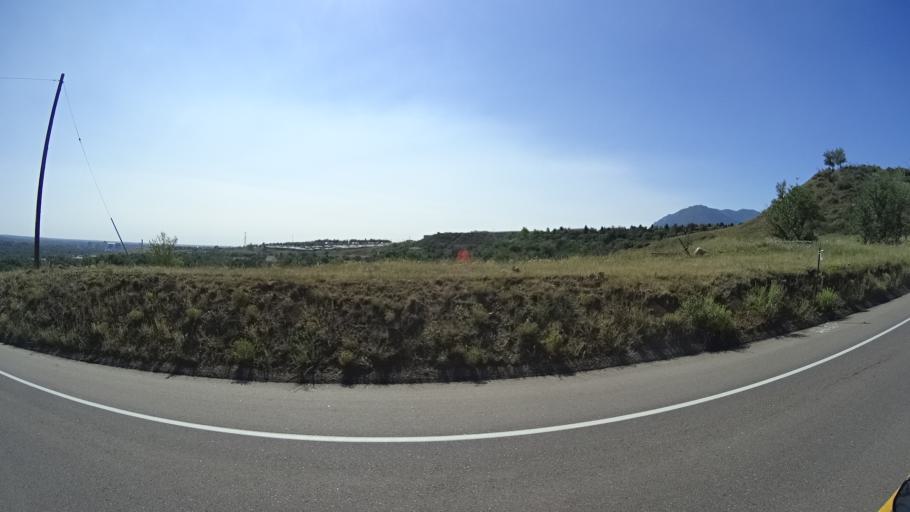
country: US
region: Colorado
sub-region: El Paso County
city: Manitou Springs
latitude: 38.8370
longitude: -104.8746
